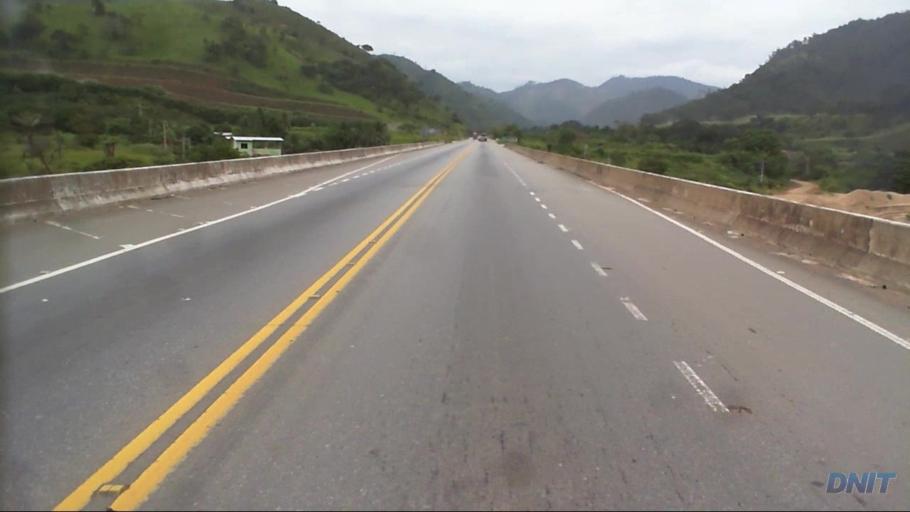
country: BR
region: Minas Gerais
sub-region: Timoteo
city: Timoteo
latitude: -19.5390
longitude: -42.6842
